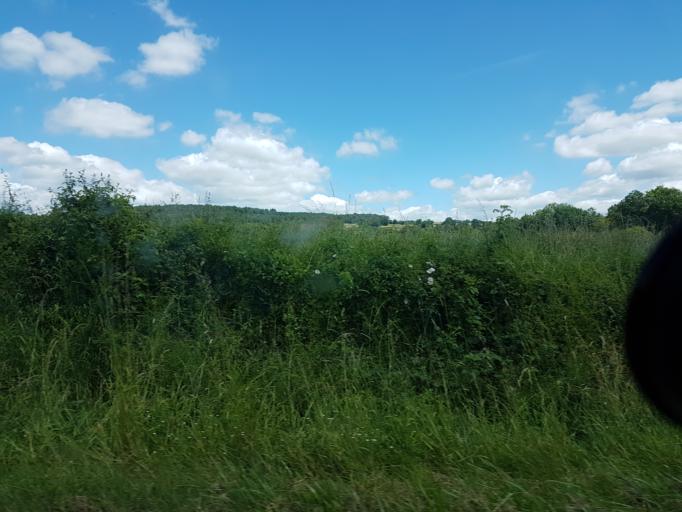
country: FR
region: Bourgogne
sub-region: Departement de Saone-et-Loire
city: Curgy
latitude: 47.0412
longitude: 4.3945
